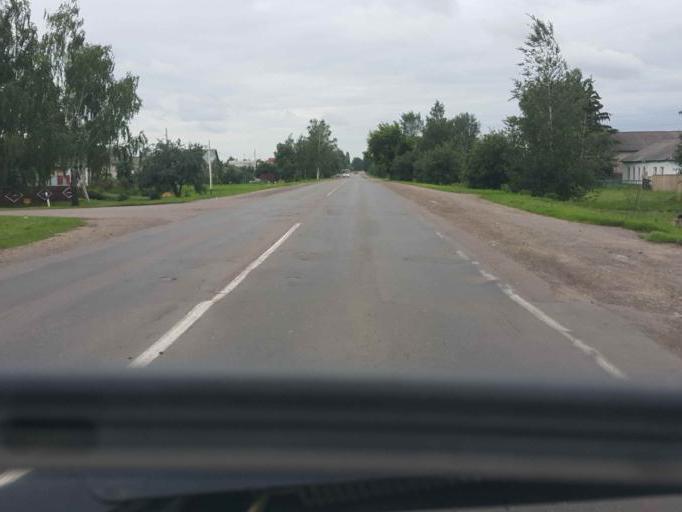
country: RU
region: Tambov
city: Zavoronezhskoye
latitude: 52.8874
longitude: 40.5609
